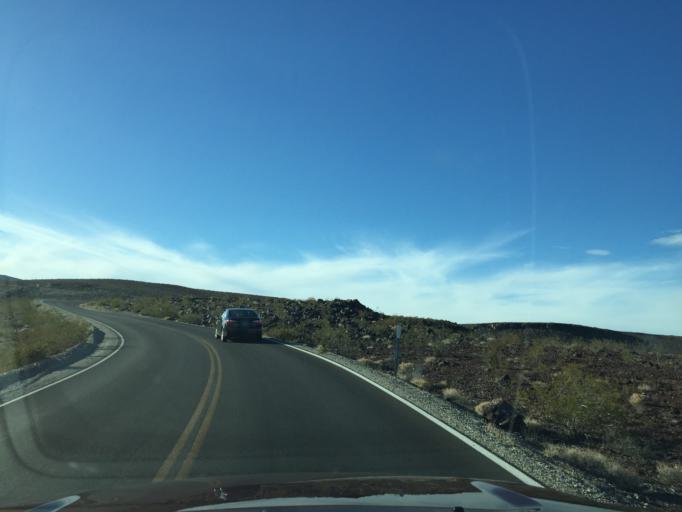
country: US
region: California
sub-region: Inyo County
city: Lone Pine
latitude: 36.3465
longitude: -117.5410
